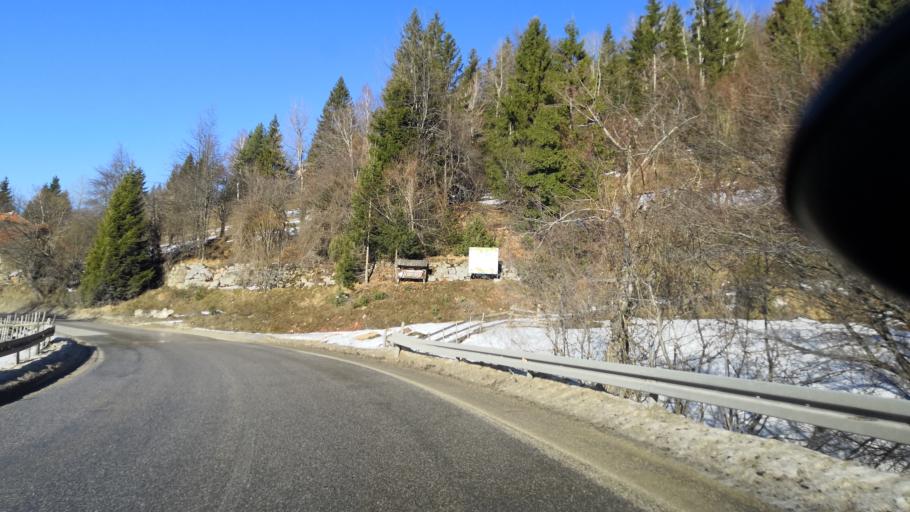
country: BA
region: Republika Srpska
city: Pale
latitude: 43.9026
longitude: 18.6378
